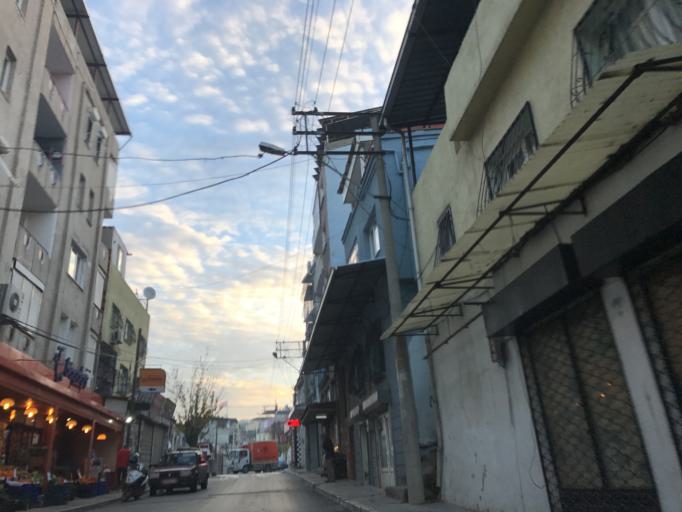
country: TR
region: Izmir
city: Izmir
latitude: 38.4117
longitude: 27.1352
